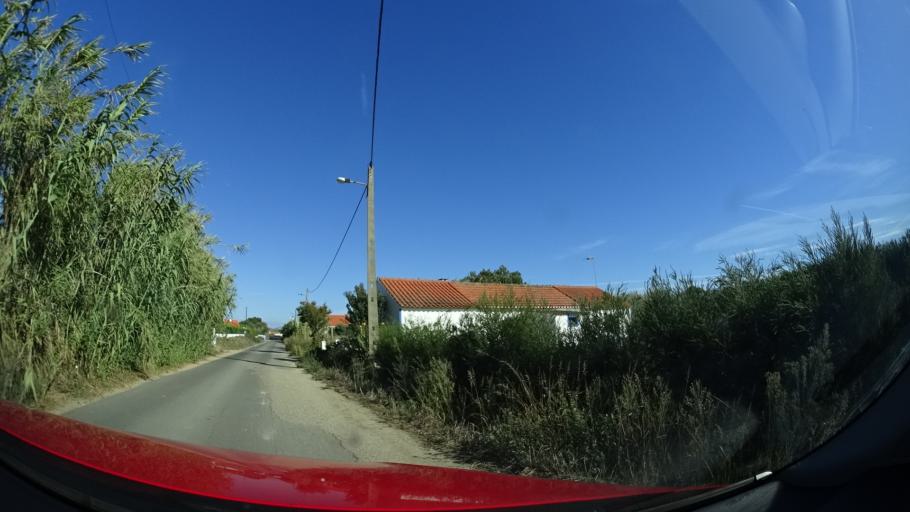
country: PT
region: Beja
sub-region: Odemira
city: Vila Nova de Milfontes
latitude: 37.5983
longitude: -8.8111
